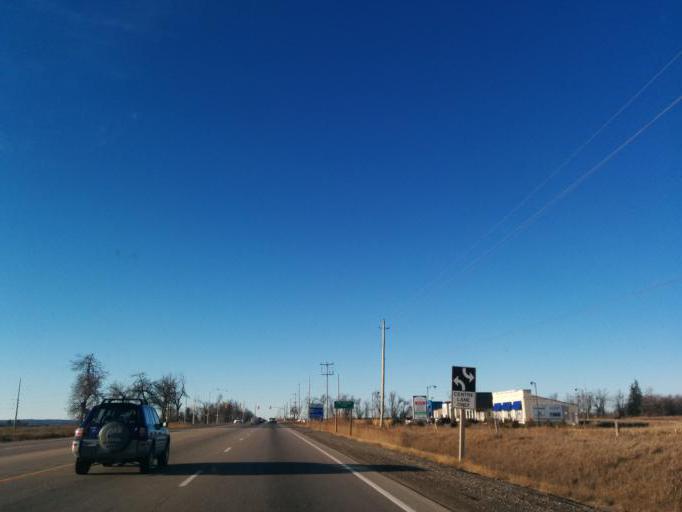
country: CA
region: Ontario
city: Brampton
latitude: 43.7521
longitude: -79.8494
